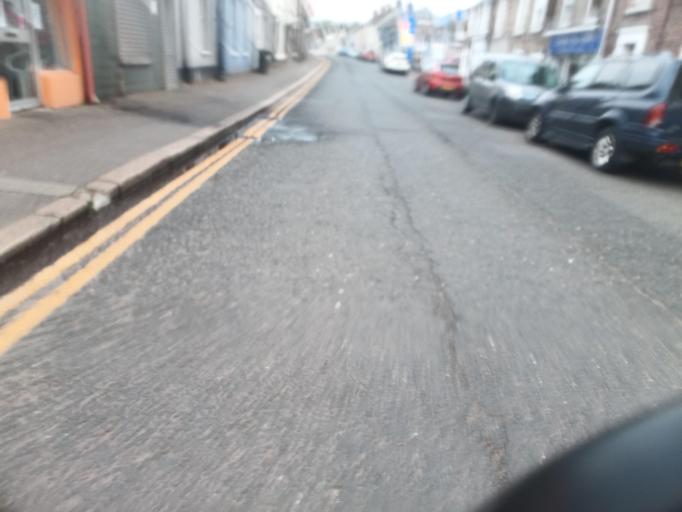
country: GB
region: Northern Ireland
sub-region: Ards District
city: Comber
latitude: 54.5514
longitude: -5.7499
